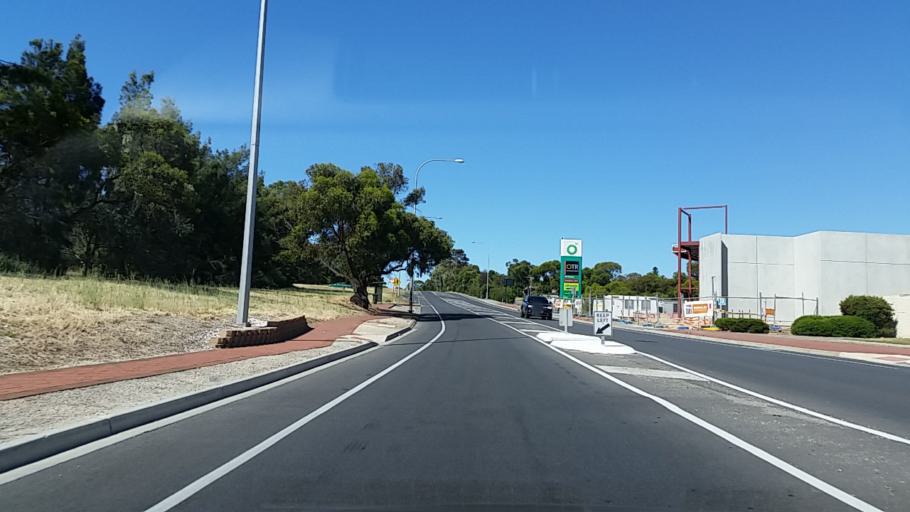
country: AU
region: South Australia
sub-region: Tea Tree Gully
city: Hope Valley
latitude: -34.8052
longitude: 138.7015
